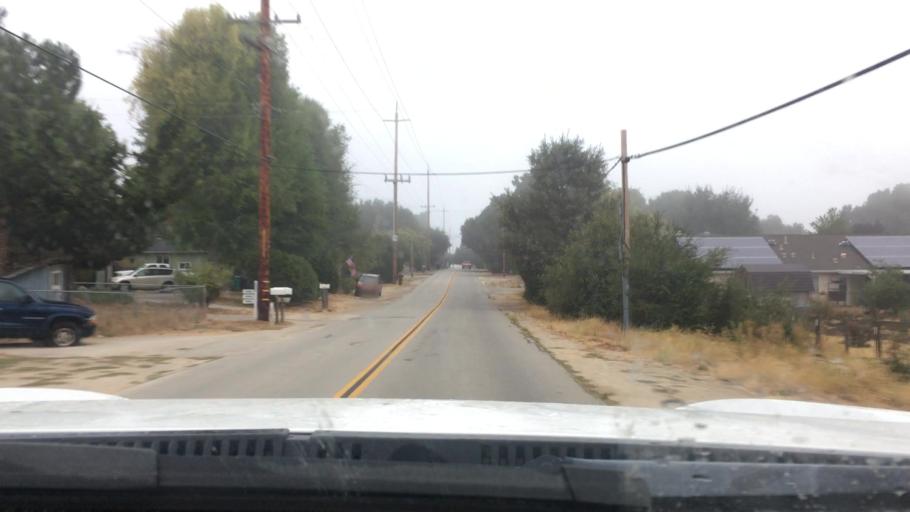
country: US
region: California
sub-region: San Luis Obispo County
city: Atascadero
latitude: 35.4837
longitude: -120.6841
